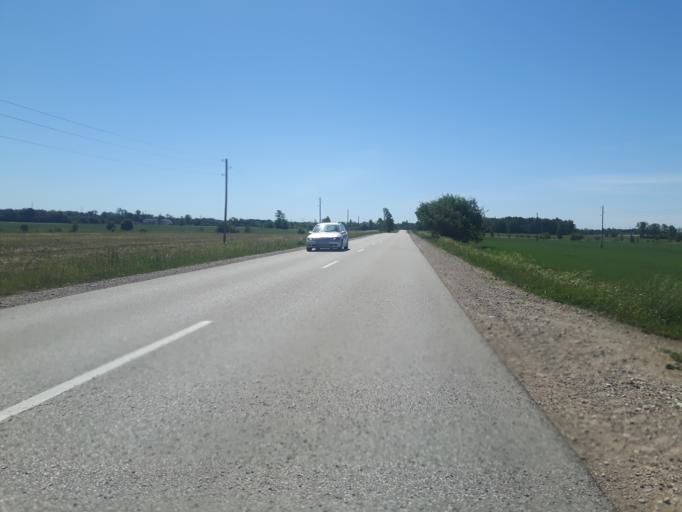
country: LV
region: Durbe
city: Liegi
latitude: 56.5731
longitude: 21.2705
